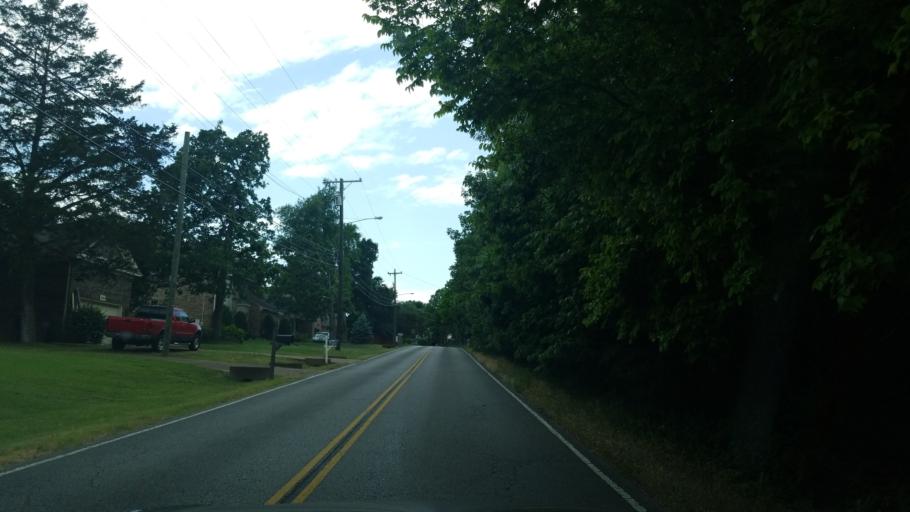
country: US
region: Tennessee
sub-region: Rutherford County
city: La Vergne
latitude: 36.0814
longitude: -86.5937
